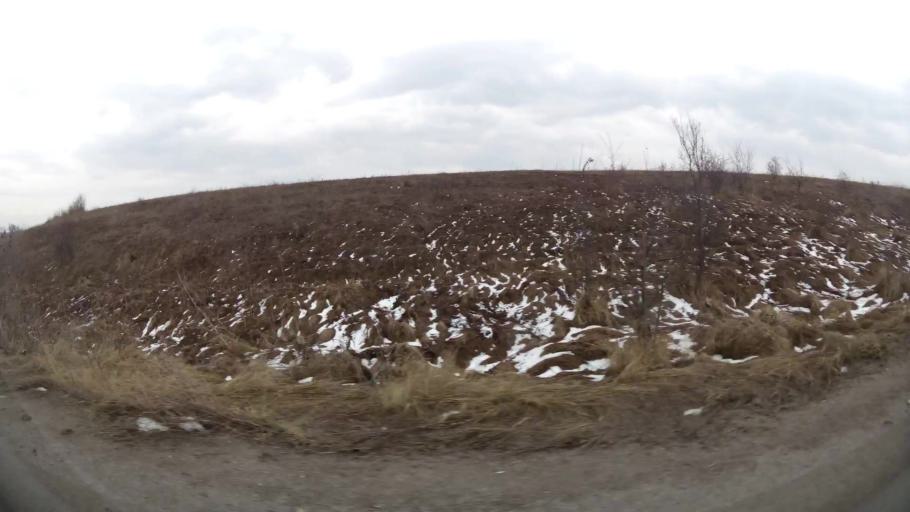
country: BG
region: Sofiya
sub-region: Obshtina Bozhurishte
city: Bozhurishte
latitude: 42.7019
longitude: 23.2206
